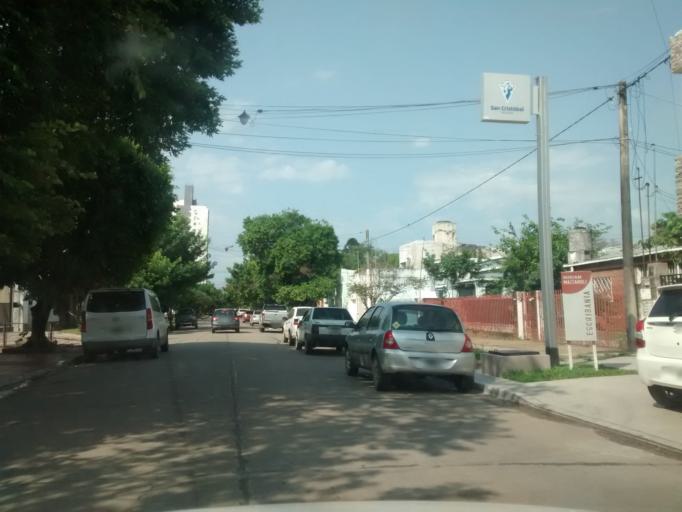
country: AR
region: Chaco
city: Resistencia
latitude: -27.4521
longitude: -58.9753
